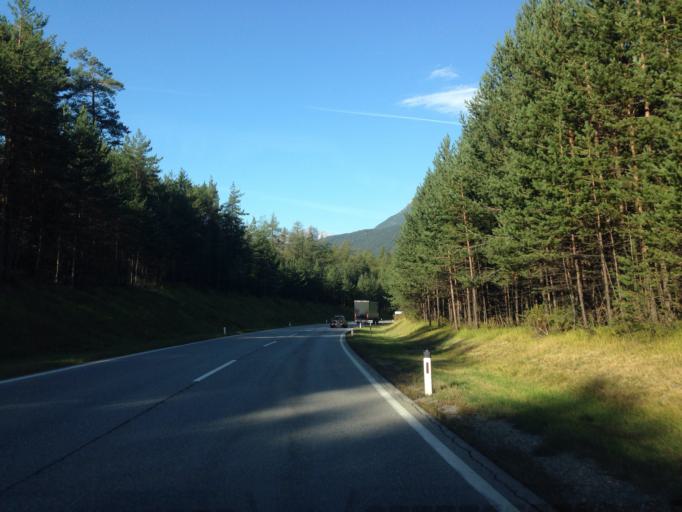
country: AT
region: Tyrol
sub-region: Politischer Bezirk Imst
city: Nassereith
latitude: 47.3062
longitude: 10.8711
